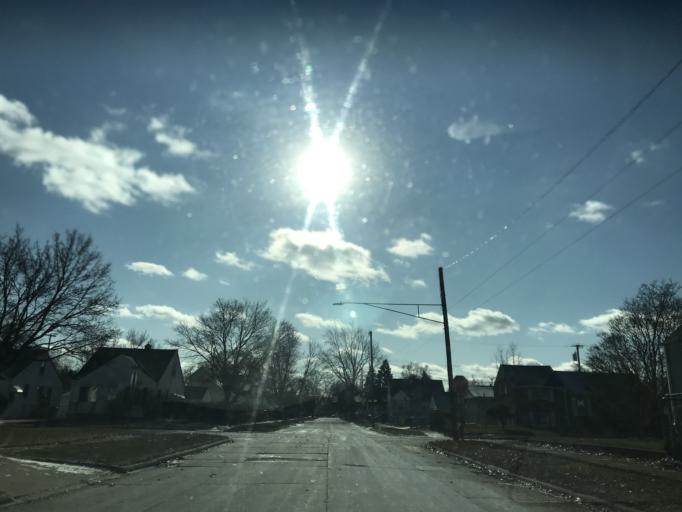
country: US
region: Michigan
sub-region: Oakland County
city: Hazel Park
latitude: 42.4714
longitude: -83.1079
